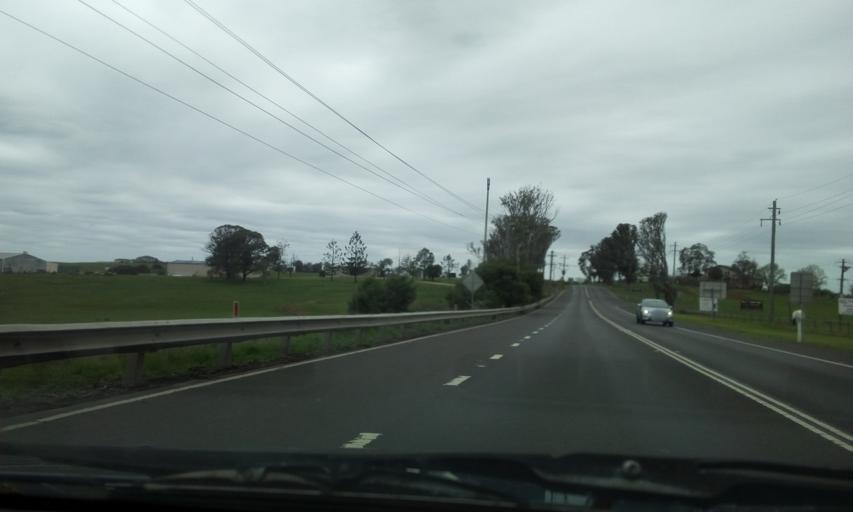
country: AU
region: New South Wales
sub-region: Liverpool
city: Luddenham
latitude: -33.8449
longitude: 150.6877
